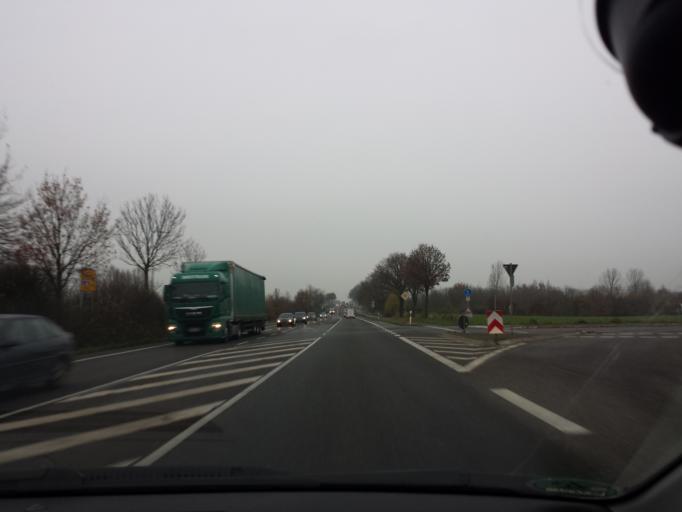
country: DE
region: North Rhine-Westphalia
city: Geilenkirchen
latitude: 51.0136
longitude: 6.1163
